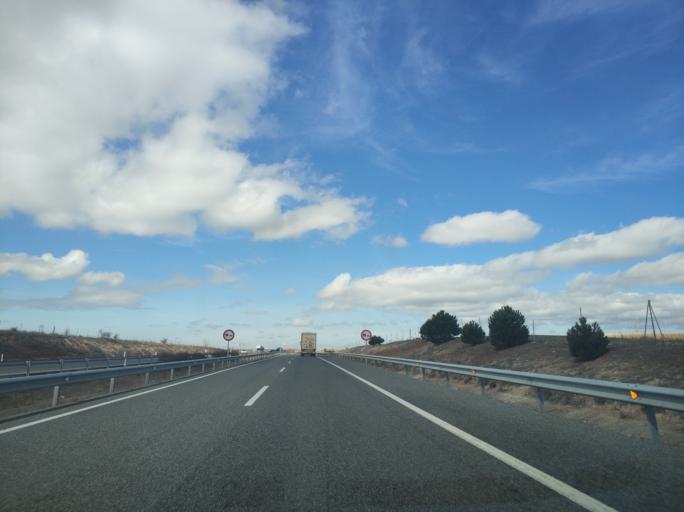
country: ES
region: Castille and Leon
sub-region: Provincia de Burgos
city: Buniel
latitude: 42.3073
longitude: -3.7956
